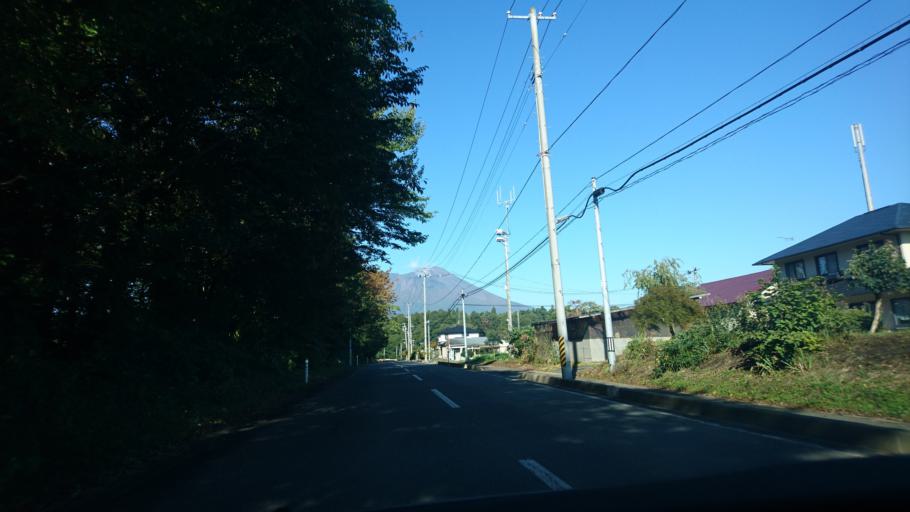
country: JP
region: Iwate
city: Morioka-shi
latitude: 39.8111
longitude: 141.1337
